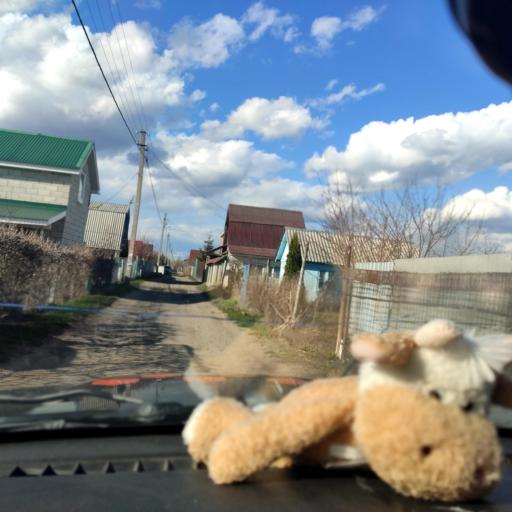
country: RU
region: Samara
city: Tol'yatti
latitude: 53.5925
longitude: 49.3072
